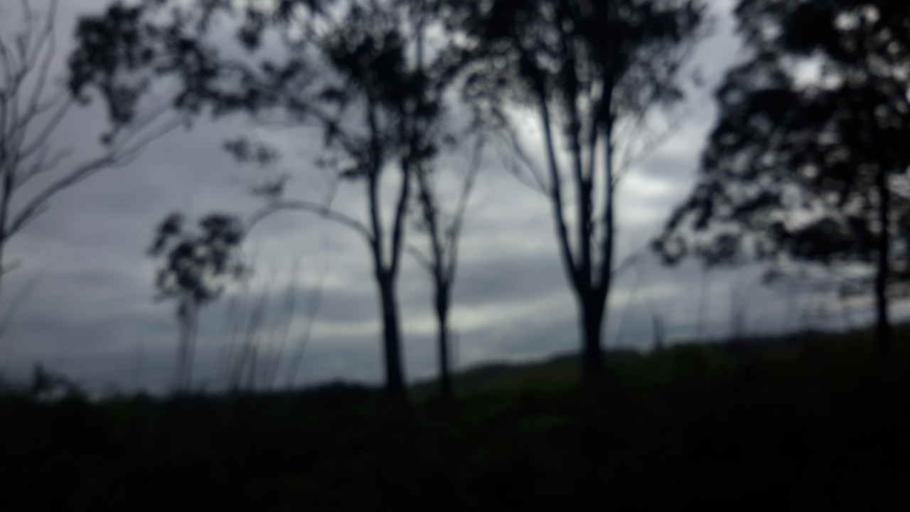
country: AU
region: New South Wales
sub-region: Campbelltown Municipality
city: Glen Alpine
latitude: -34.1193
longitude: 150.7389
